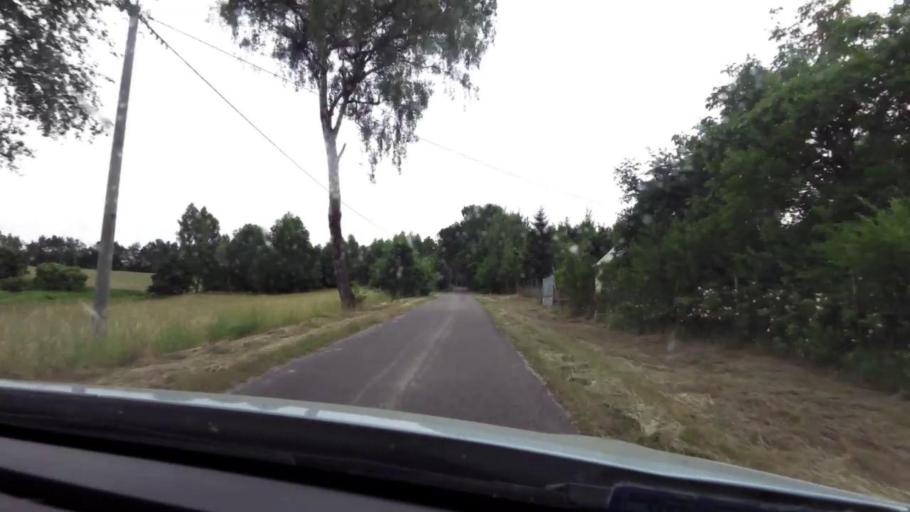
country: PL
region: Pomeranian Voivodeship
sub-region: Powiat bytowski
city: Trzebielino
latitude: 54.2460
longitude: 17.0014
